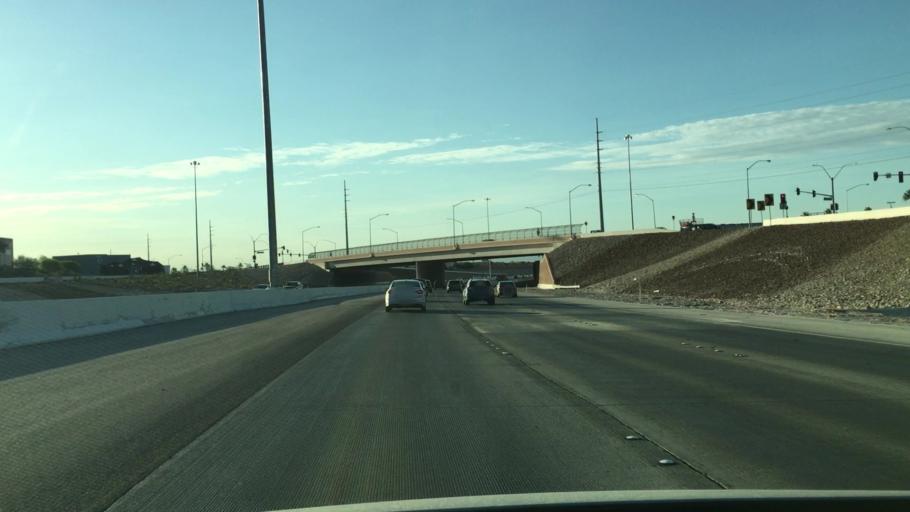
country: US
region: Nevada
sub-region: Clark County
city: Summerlin South
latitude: 36.1163
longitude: -115.3048
